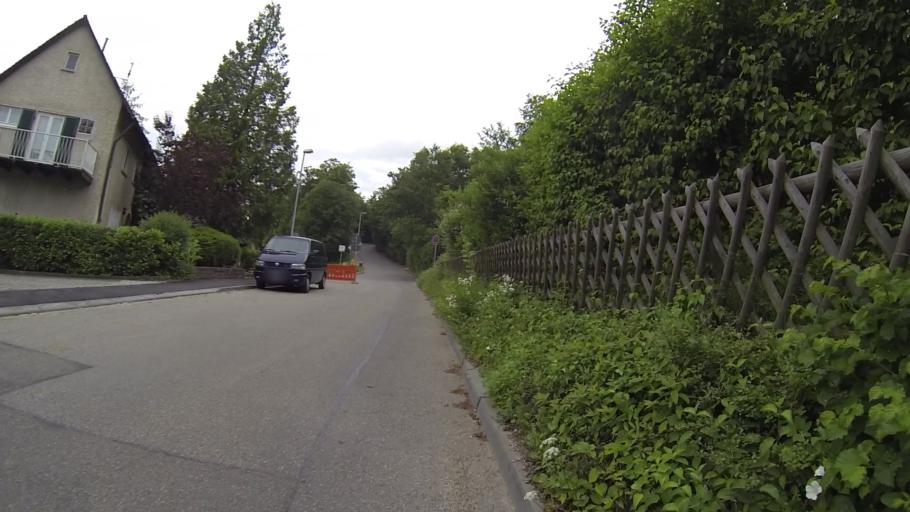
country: DE
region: Baden-Wuerttemberg
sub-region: Tuebingen Region
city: Dornstadt
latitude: 48.4198
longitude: 9.8904
